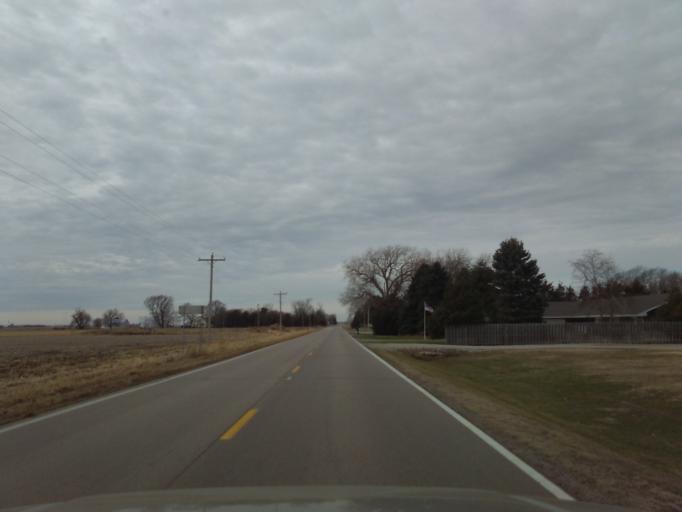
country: US
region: Nebraska
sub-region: Hall County
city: Grand Island
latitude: 40.7709
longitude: -98.4121
